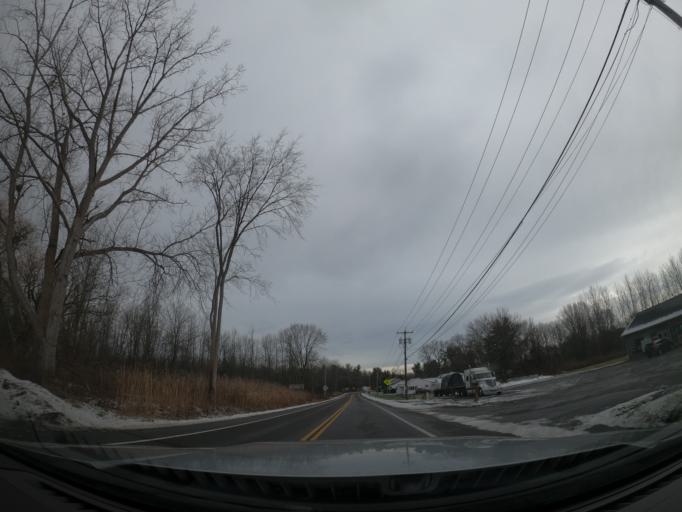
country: US
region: New York
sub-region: Onondaga County
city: Minoa
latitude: 43.1159
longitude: -76.0034
